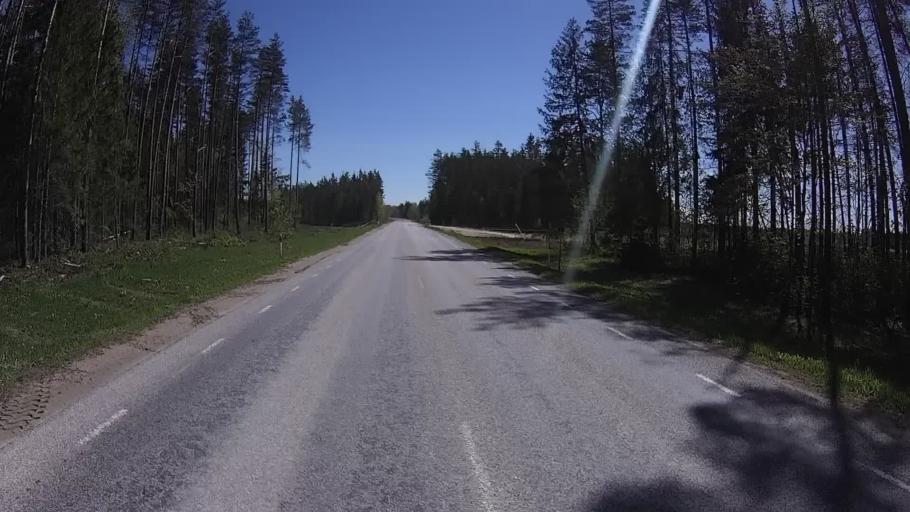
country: EE
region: Harju
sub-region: Raasiku vald
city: Raasiku
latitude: 59.1617
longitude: 25.1810
